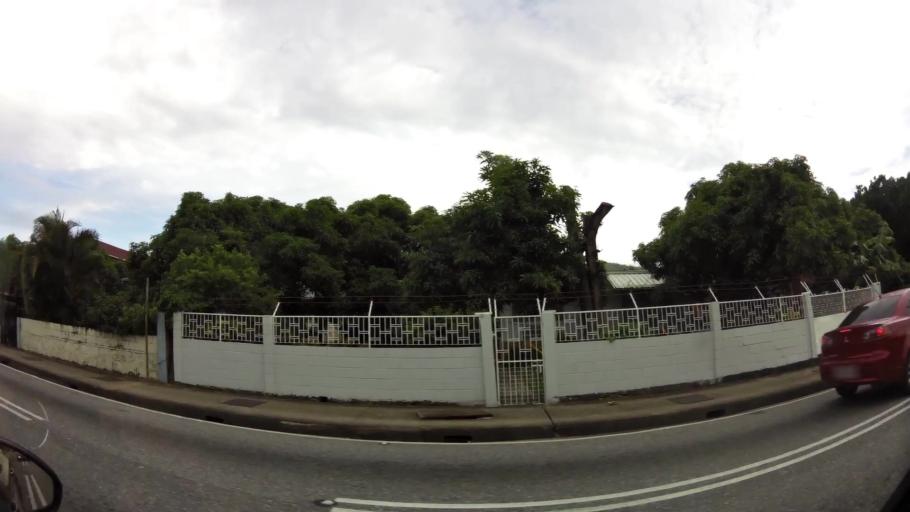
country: TT
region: Tunapuna/Piarco
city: Tunapuna
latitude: 10.6500
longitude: -61.4309
